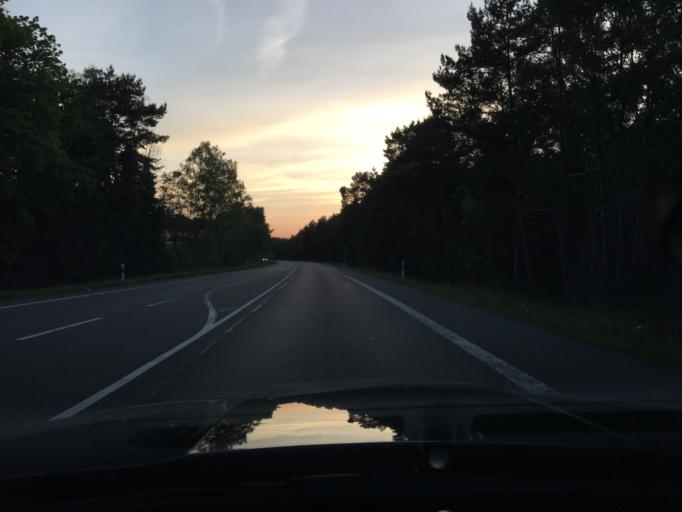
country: DE
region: North Rhine-Westphalia
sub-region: Regierungsbezirk Munster
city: Ladbergen
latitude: 52.1437
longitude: 7.7548
